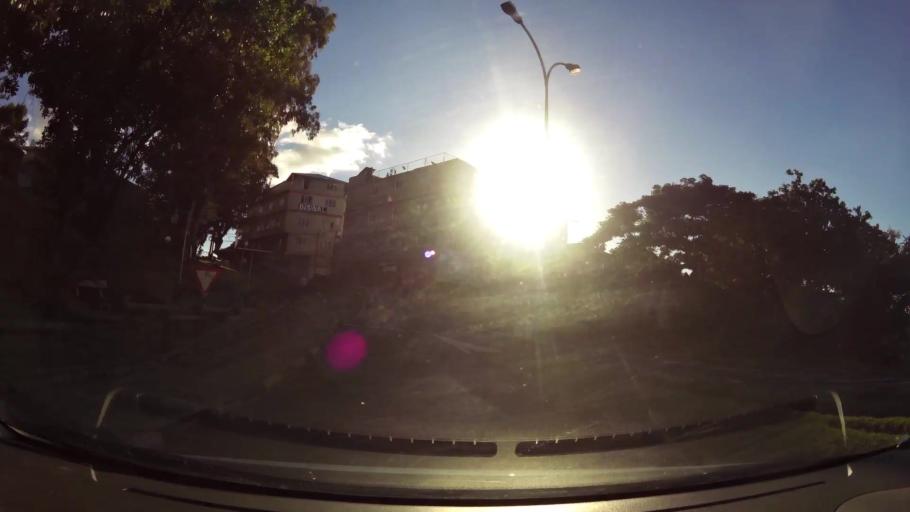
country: MU
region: Moka
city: Pailles
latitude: -20.1830
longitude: 57.4699
